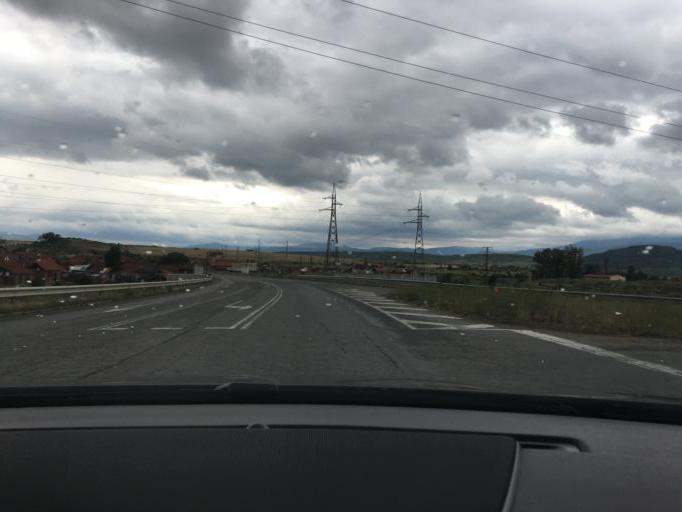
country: BG
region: Kyustendil
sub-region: Obshtina Kyustendil
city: Kyustendil
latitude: 42.2957
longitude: 22.7190
